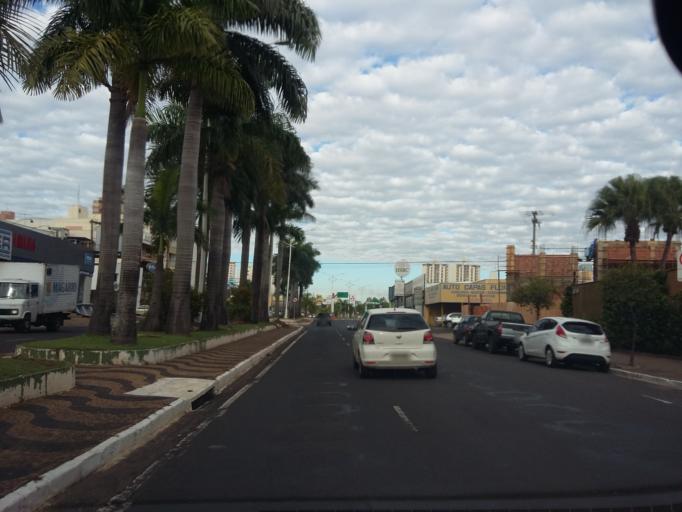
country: BR
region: Sao Paulo
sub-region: Sao Jose Do Rio Preto
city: Sao Jose do Rio Preto
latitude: -20.8159
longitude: -49.3930
